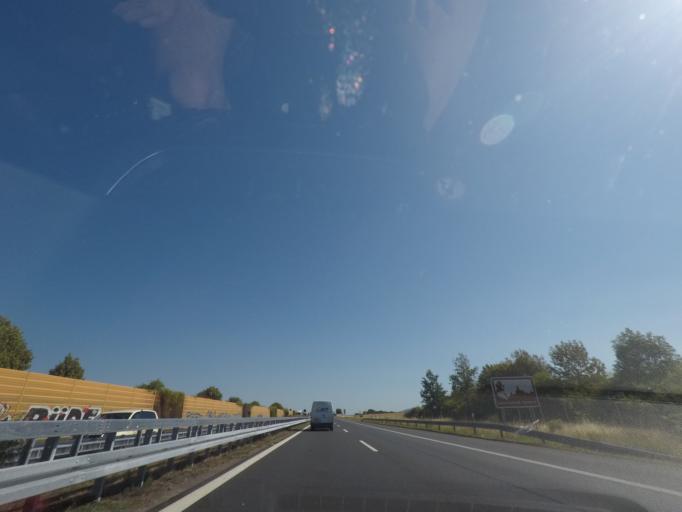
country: DE
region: Saxony
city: Ottendorf-Okrilla
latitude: 51.1659
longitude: 13.8006
